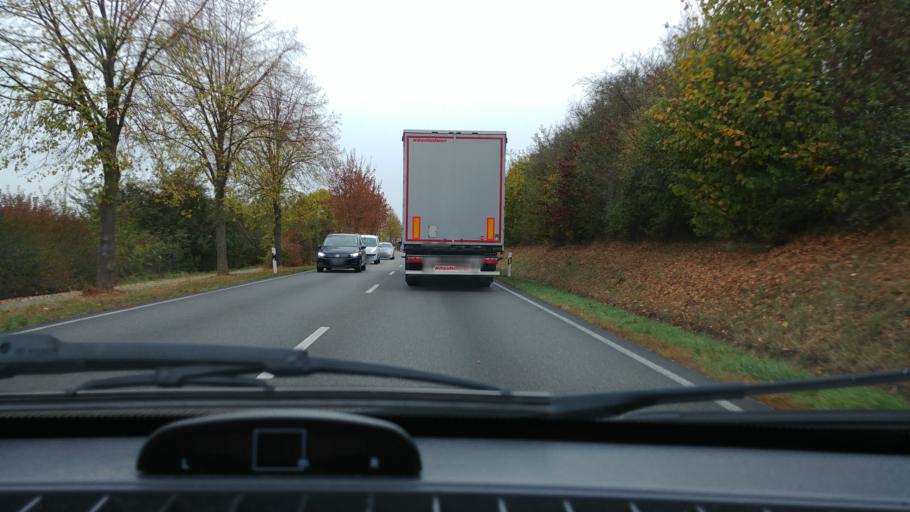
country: DE
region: Baden-Wuerttemberg
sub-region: Regierungsbezirk Stuttgart
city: Bad Mergentheim
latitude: 49.5183
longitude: 9.7496
